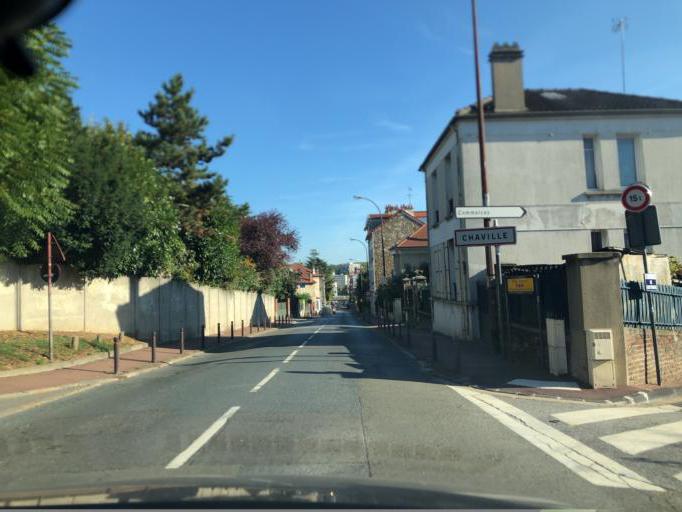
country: FR
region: Ile-de-France
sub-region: Departement des Hauts-de-Seine
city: Chaville
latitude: 48.7970
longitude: 2.1828
